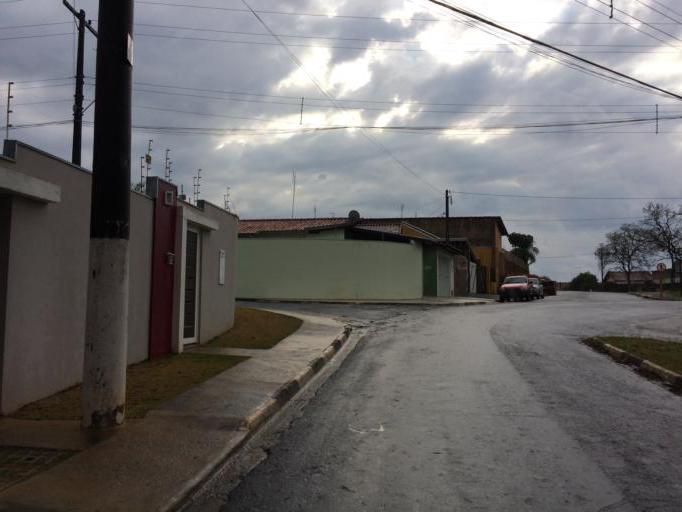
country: BR
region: Sao Paulo
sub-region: Capao Bonito
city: Capao Bonito
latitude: -24.0145
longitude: -48.3426
